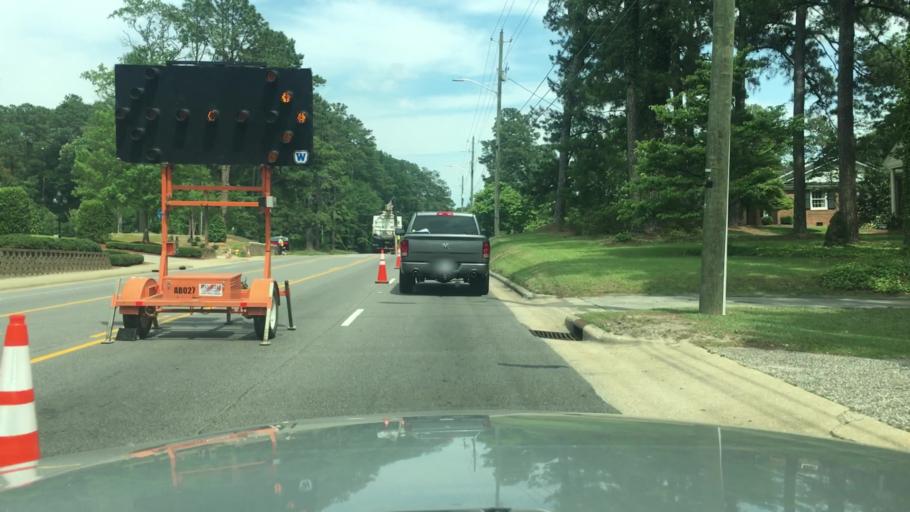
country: US
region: North Carolina
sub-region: Cumberland County
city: Fayetteville
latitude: 35.0638
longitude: -78.9241
